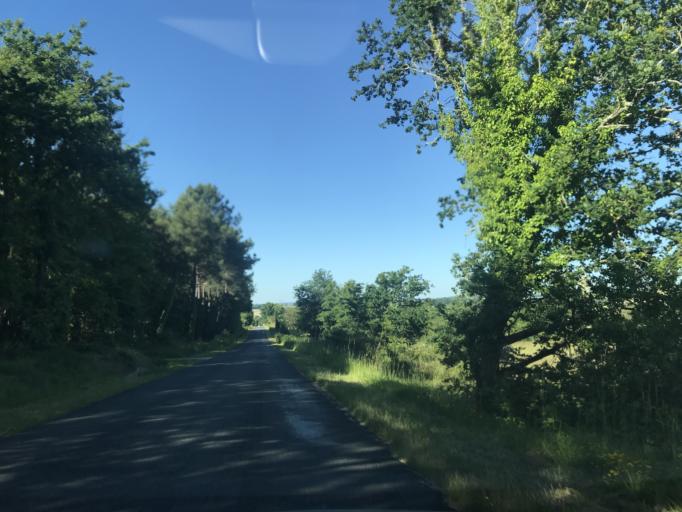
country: FR
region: Poitou-Charentes
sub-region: Departement de la Charente
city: Chalais
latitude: 45.2403
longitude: -0.0041
